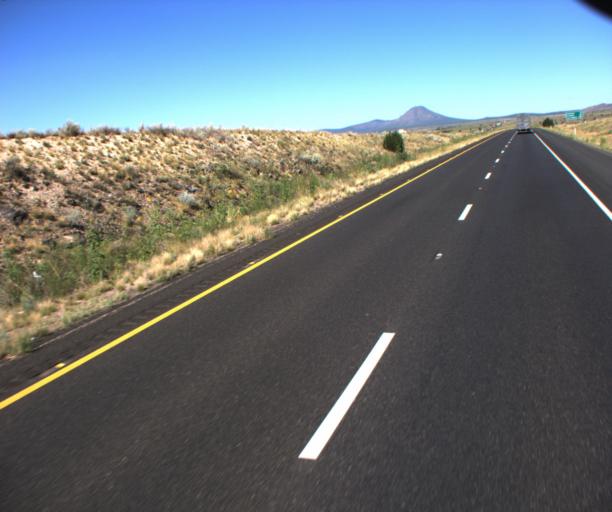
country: US
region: Arizona
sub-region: Yavapai County
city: Paulden
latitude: 35.2317
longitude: -112.6004
